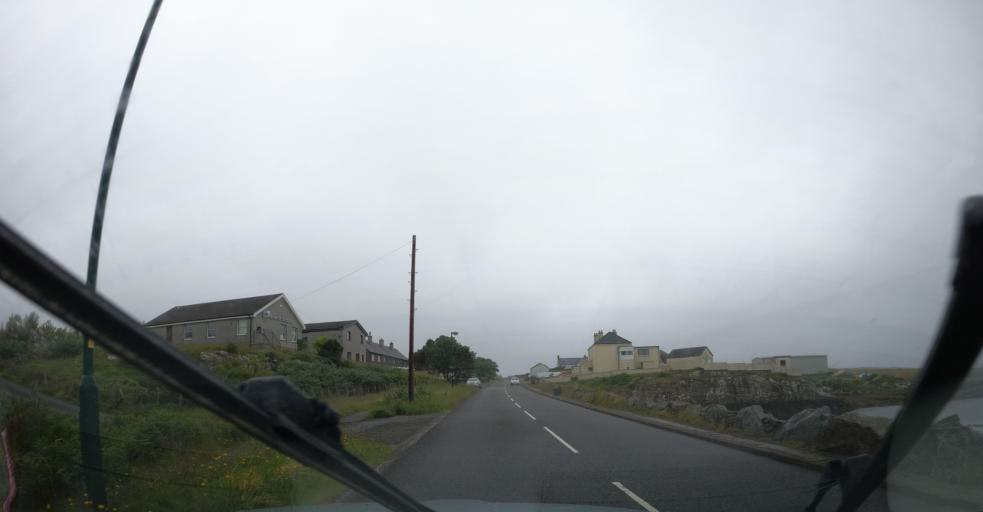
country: GB
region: Scotland
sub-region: Eilean Siar
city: Isle of North Uist
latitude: 57.5990
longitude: -7.1600
